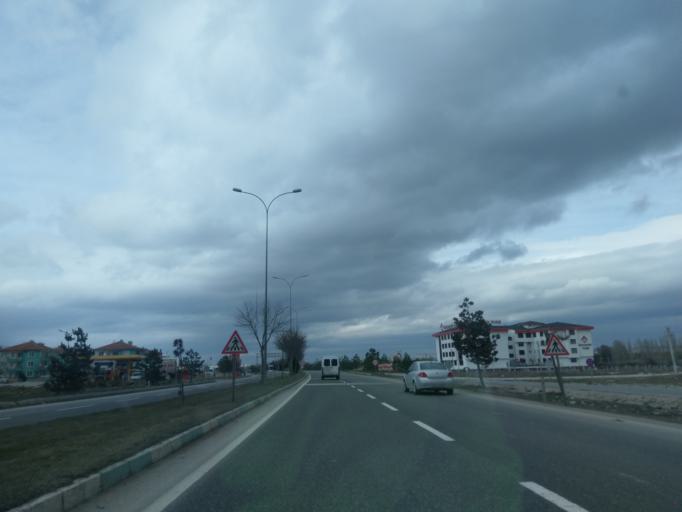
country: TR
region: Kuetahya
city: Kutahya
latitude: 39.4081
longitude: 30.0250
